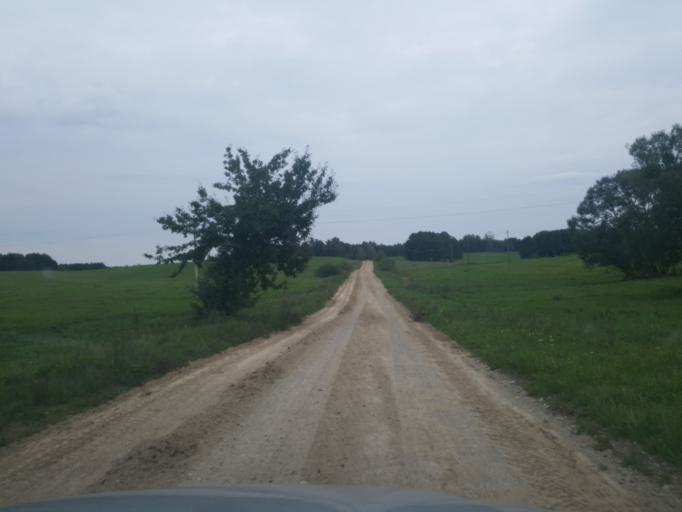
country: LT
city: Veisiejai
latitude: 54.1225
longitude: 23.5838
